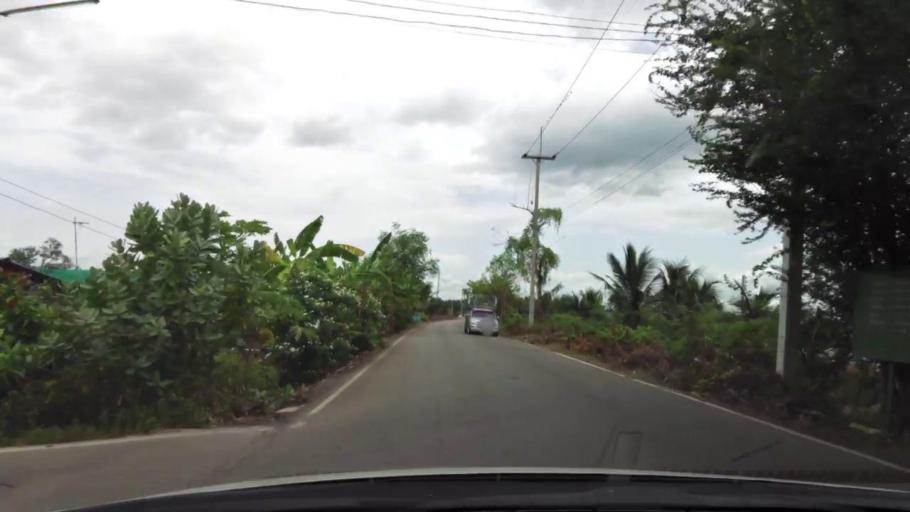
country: TH
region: Samut Sakhon
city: Ban Phaeo
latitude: 13.5744
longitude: 100.0299
